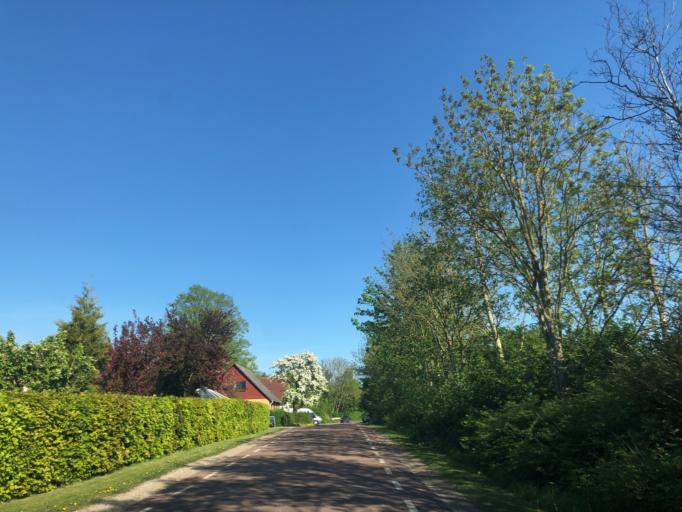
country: DK
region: Zealand
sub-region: Ringsted Kommune
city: Ringsted
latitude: 55.4488
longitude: 11.7265
